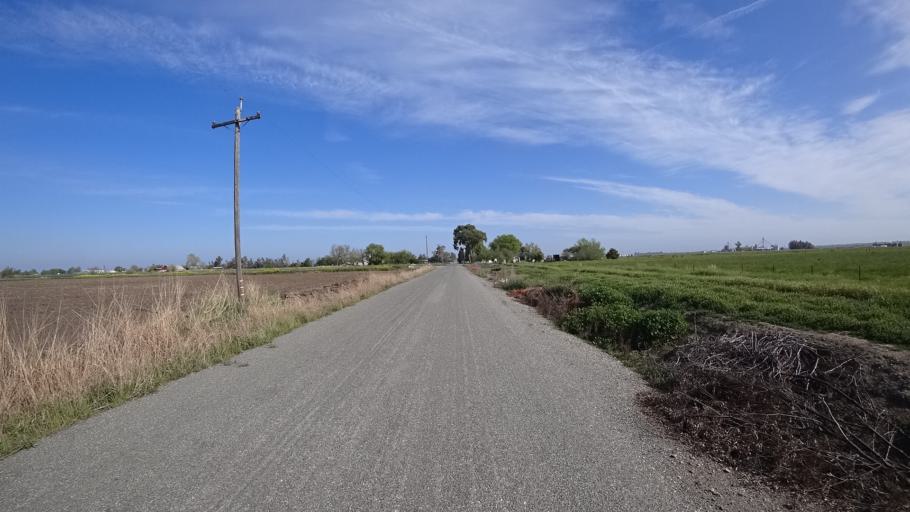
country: US
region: California
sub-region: Glenn County
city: Willows
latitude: 39.5750
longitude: -122.0371
